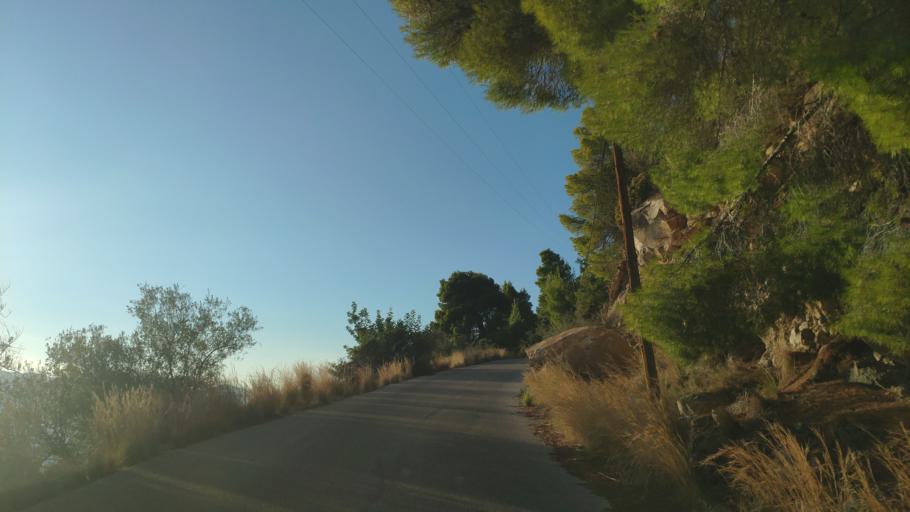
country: GR
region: Attica
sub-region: Nomos Piraios
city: Megalochori
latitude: 37.6022
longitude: 23.3330
